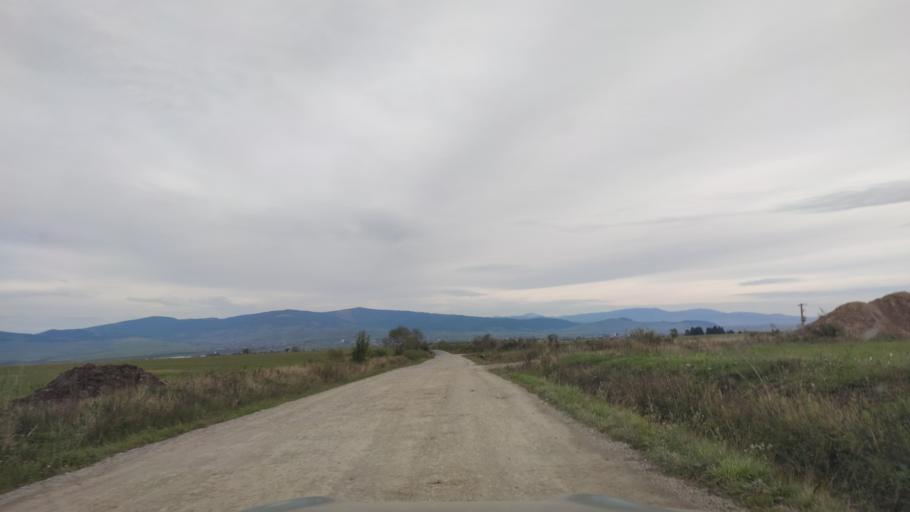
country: RO
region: Harghita
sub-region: Comuna Remetea
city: Remetea
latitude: 46.8084
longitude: 25.4051
